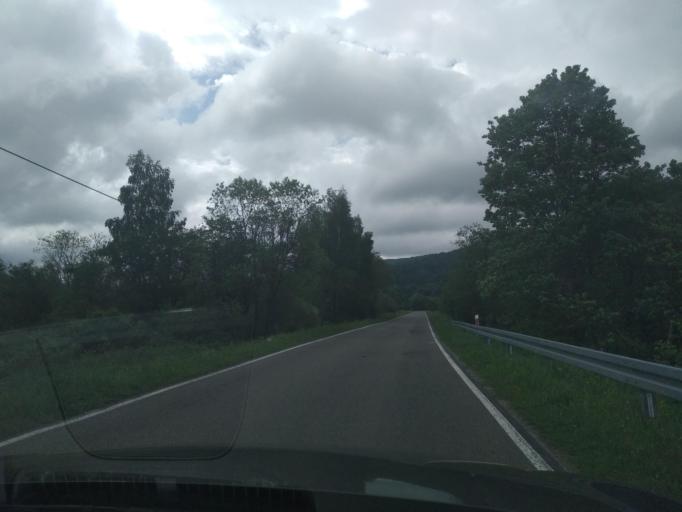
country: PL
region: Subcarpathian Voivodeship
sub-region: Powiat bieszczadzki
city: Lutowiska
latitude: 49.0869
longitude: 22.6507
